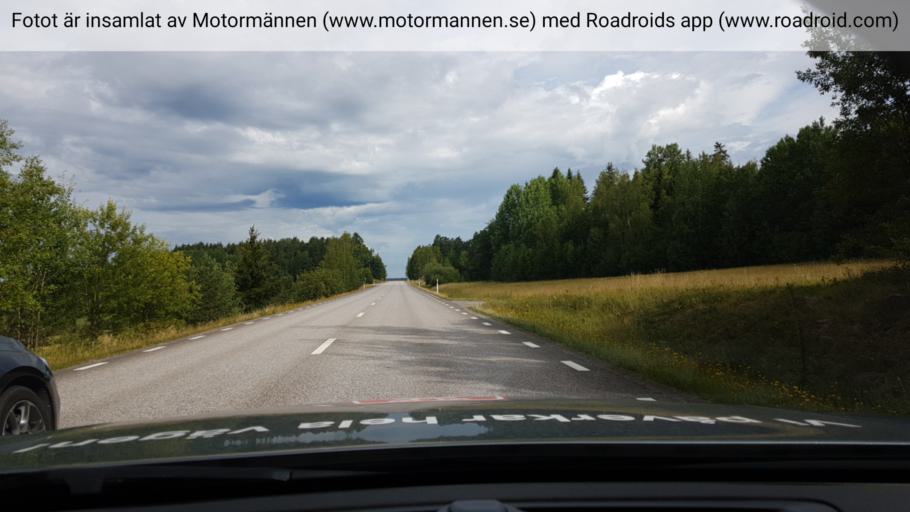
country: SE
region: Uppsala
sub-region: Heby Kommun
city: Heby
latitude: 59.9083
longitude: 16.8928
